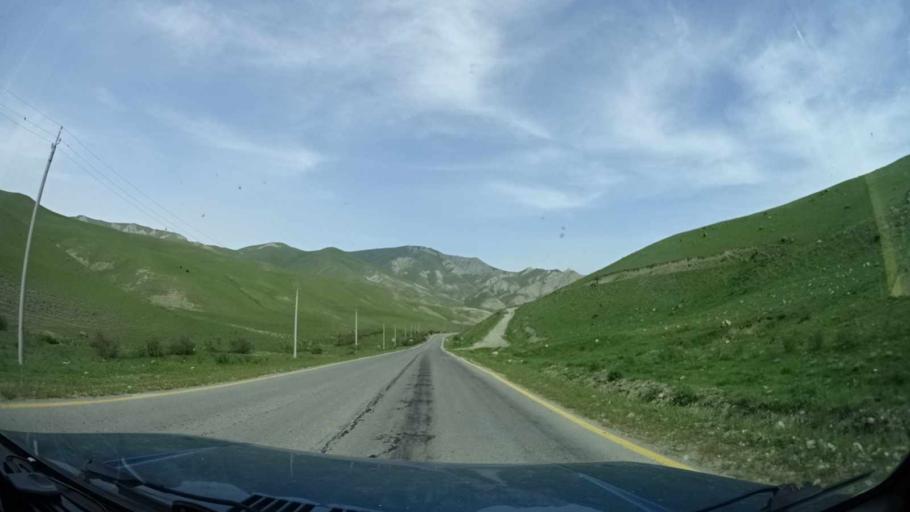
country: AZ
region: Xizi
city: Khyzy
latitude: 40.9073
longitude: 49.1248
